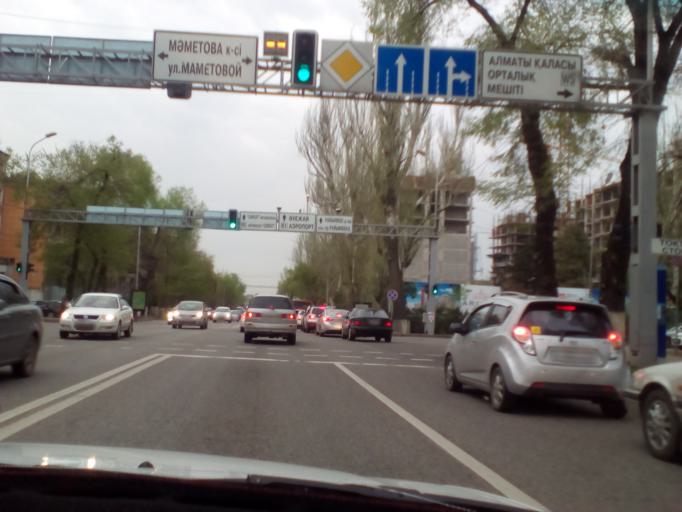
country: KZ
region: Almaty Qalasy
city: Almaty
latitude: 43.2670
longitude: 76.9452
